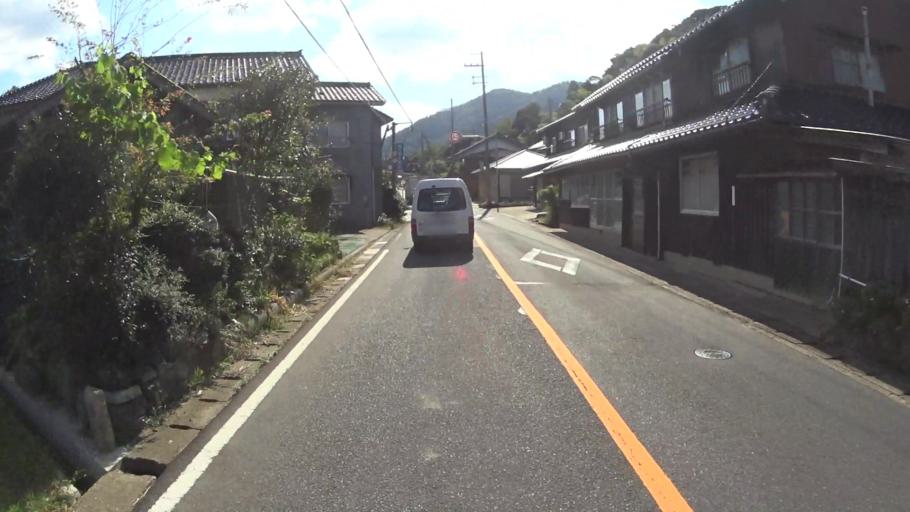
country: JP
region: Kyoto
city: Miyazu
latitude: 35.7523
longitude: 135.1687
